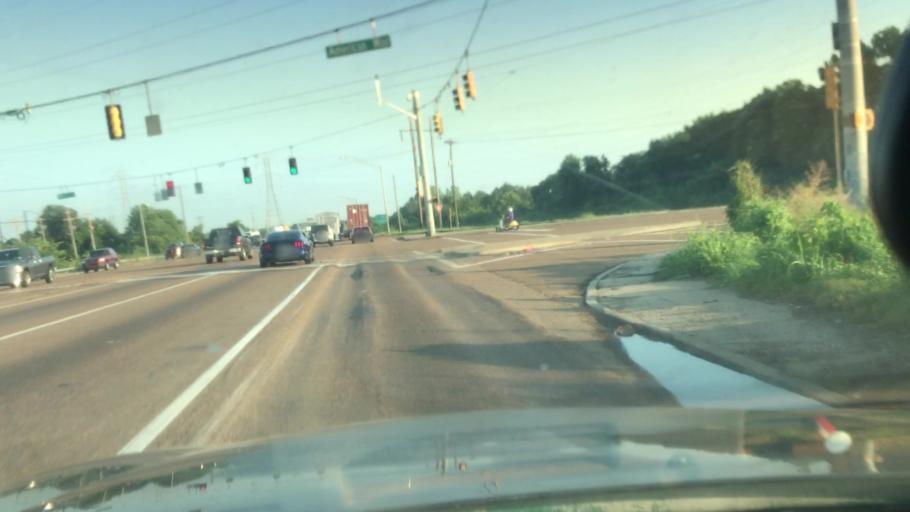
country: US
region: Tennessee
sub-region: Shelby County
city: New South Memphis
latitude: 35.0763
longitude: -89.9507
